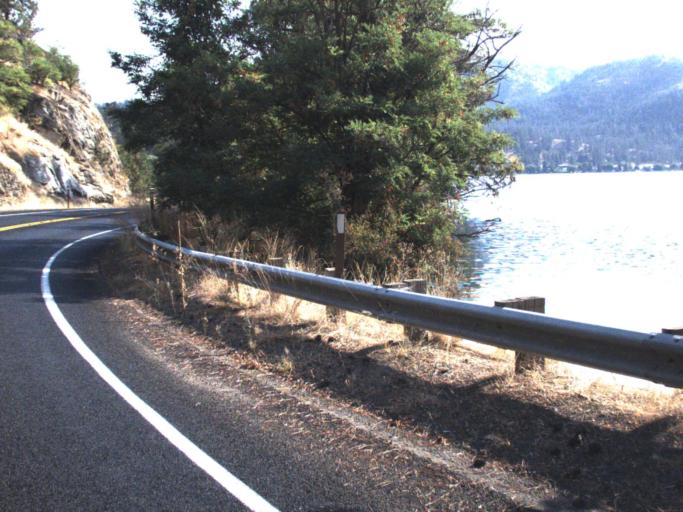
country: US
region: Washington
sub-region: Spokane County
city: Deer Park
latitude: 47.8892
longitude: -117.6885
